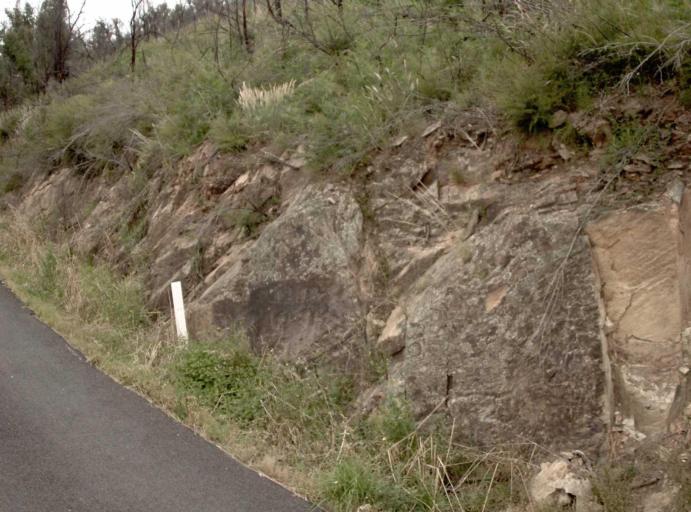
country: AU
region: Victoria
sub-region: Wellington
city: Heyfield
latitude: -37.8522
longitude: 146.7071
